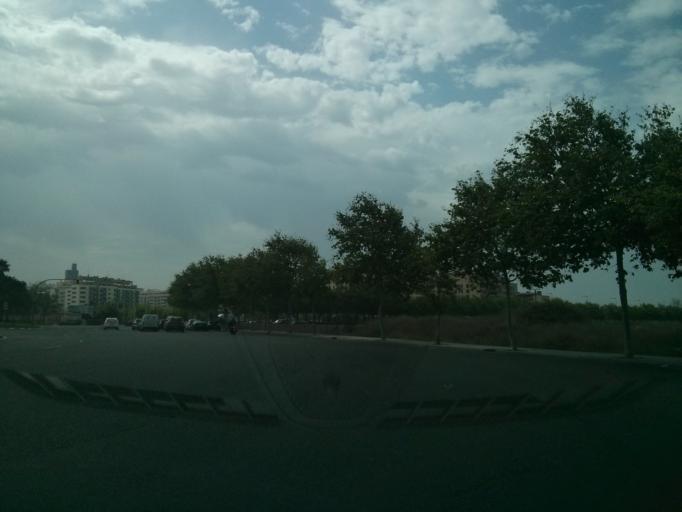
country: ES
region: Valencia
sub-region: Provincia de Valencia
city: Tavernes Blanques
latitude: 39.4981
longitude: -0.3848
